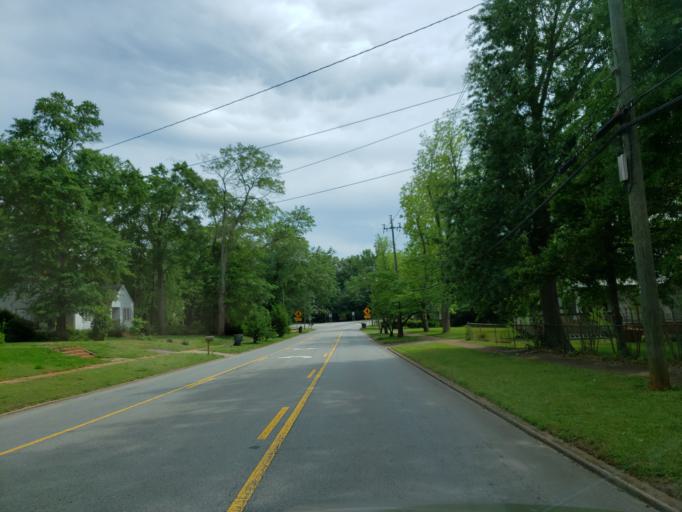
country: US
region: Georgia
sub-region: Monroe County
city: Forsyth
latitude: 33.0310
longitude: -83.9385
